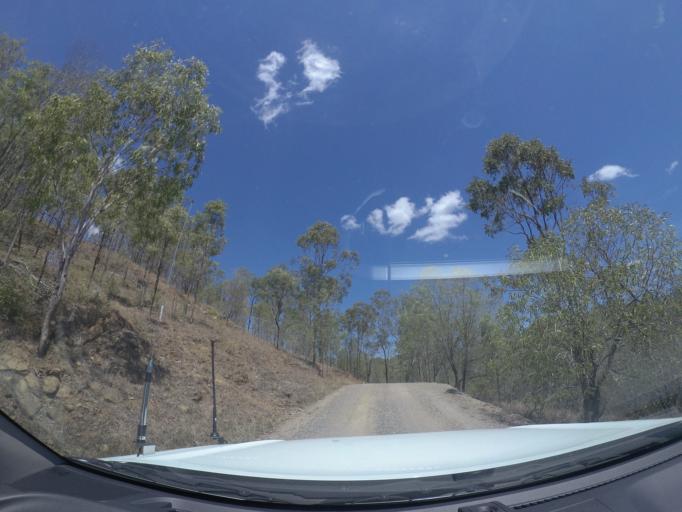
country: AU
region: Queensland
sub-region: Ipswich
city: Springfield Lakes
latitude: -27.8159
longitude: 152.8503
